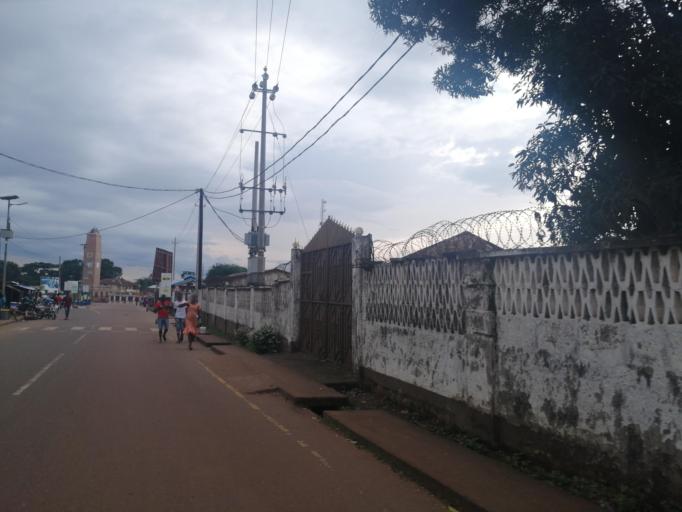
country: SL
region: Northern Province
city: Port Loko
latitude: 8.7653
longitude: -12.7843
